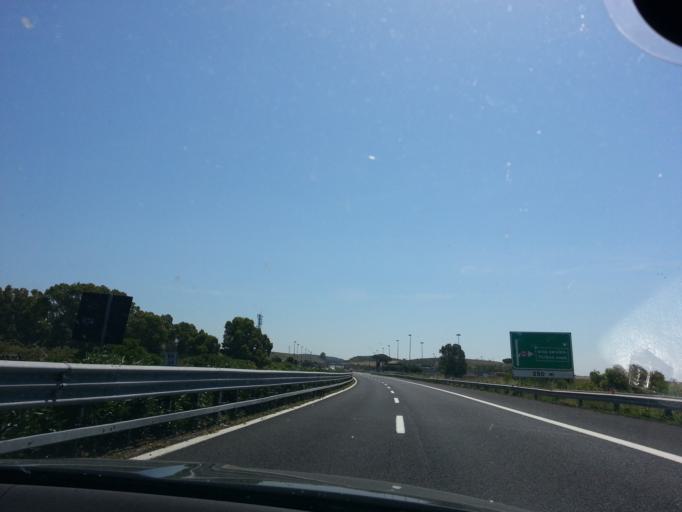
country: IT
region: Latium
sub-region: Citta metropolitana di Roma Capitale
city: Santa Marinella
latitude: 42.0307
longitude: 11.9570
